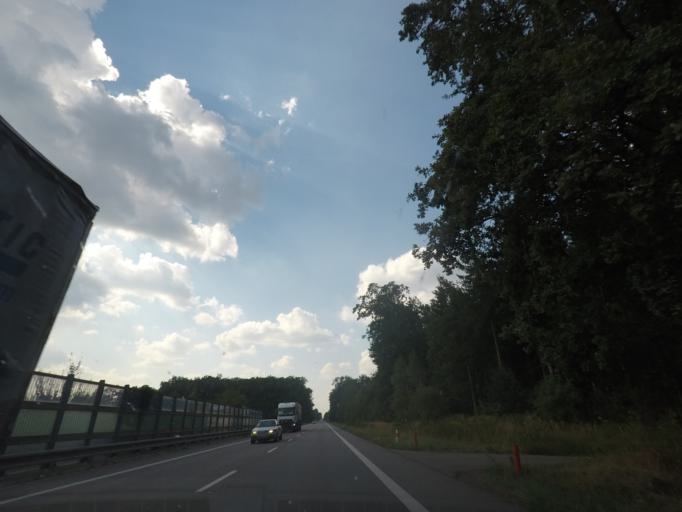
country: CZ
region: Kralovehradecky
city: Trebechovice pod Orebem
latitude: 50.1755
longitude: 16.0311
